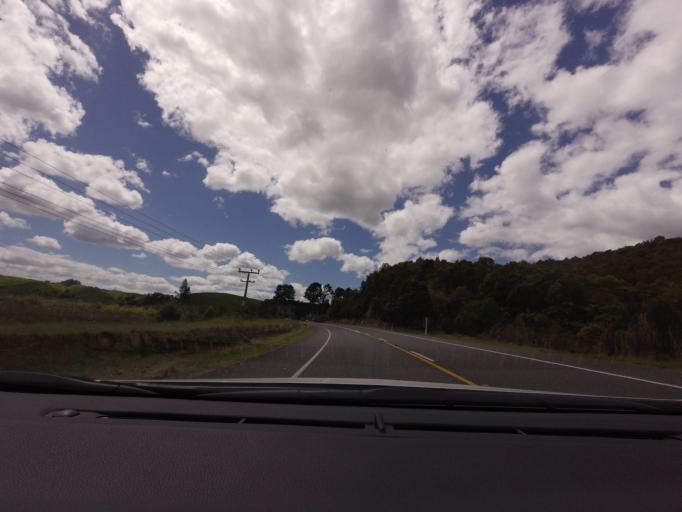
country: NZ
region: Bay of Plenty
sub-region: Rotorua District
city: Rotorua
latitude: -38.3130
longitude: 176.3775
